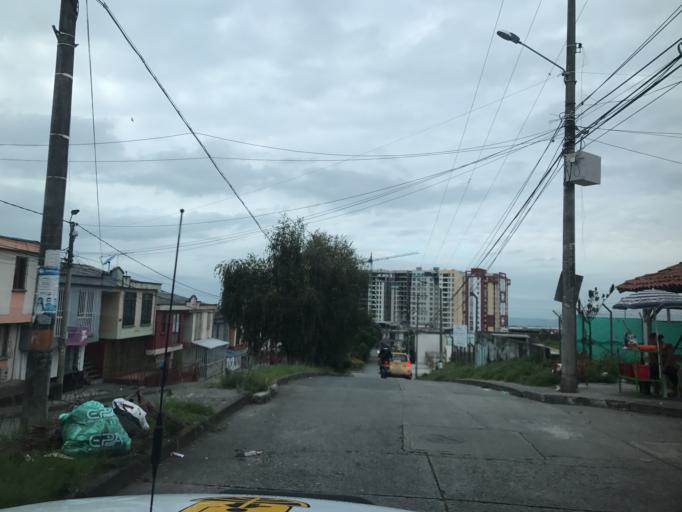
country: CO
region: Quindio
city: Armenia
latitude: 4.5352
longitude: -75.6989
